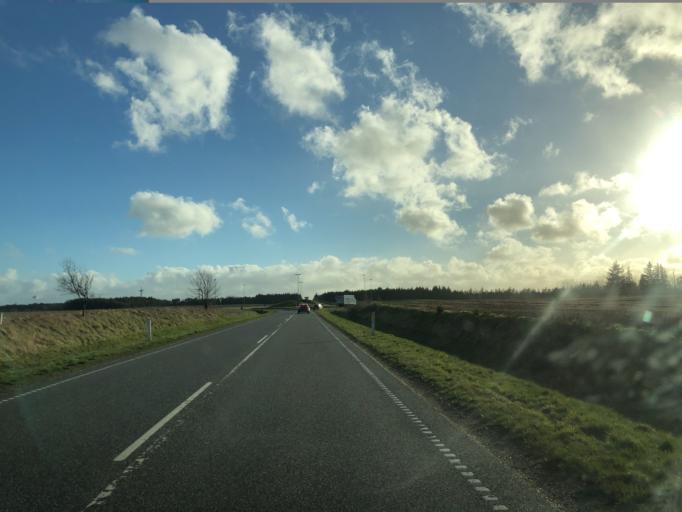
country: DK
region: Central Jutland
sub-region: Herning Kommune
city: Vildbjerg
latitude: 56.1844
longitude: 8.7036
